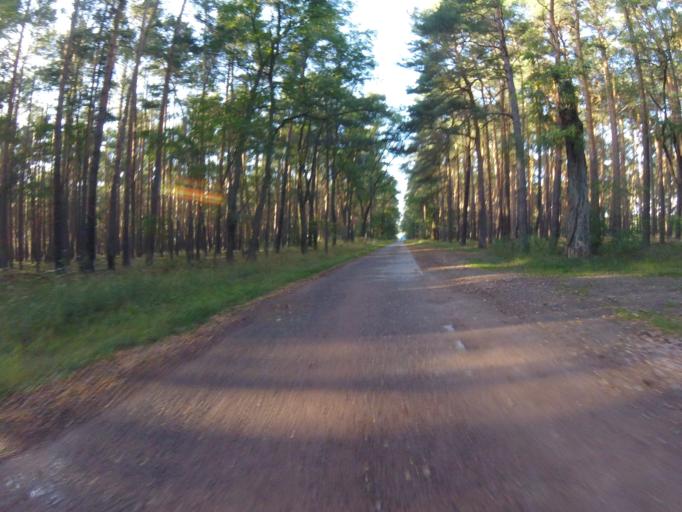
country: DE
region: Brandenburg
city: Munchehofe
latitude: 52.2129
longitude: 13.7722
